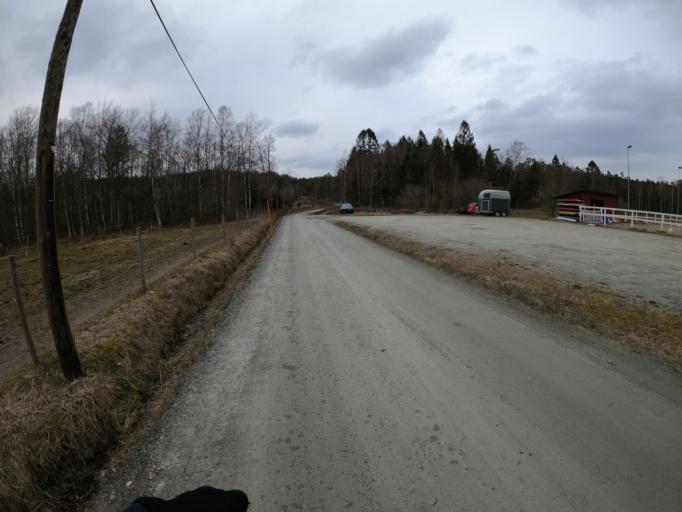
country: SE
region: Vaestra Goetaland
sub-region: Harryda Kommun
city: Molnlycke
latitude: 57.6329
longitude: 12.1029
